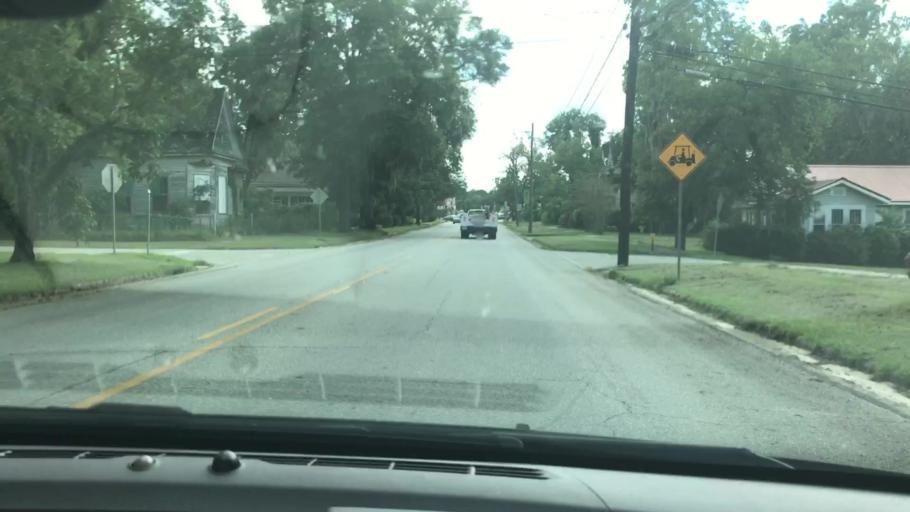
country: US
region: Georgia
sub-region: Clay County
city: Fort Gaines
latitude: 31.6090
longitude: -85.0498
